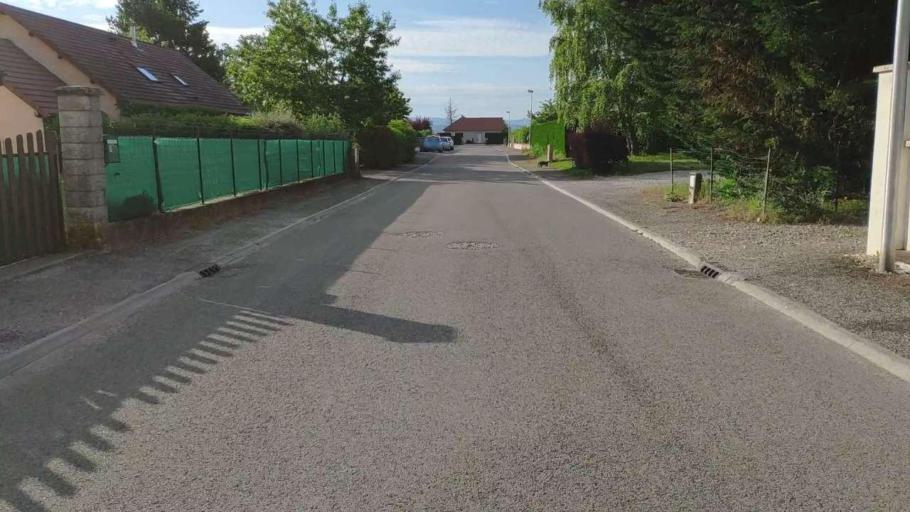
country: FR
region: Franche-Comte
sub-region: Departement du Jura
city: Bletterans
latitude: 46.7504
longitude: 5.4456
